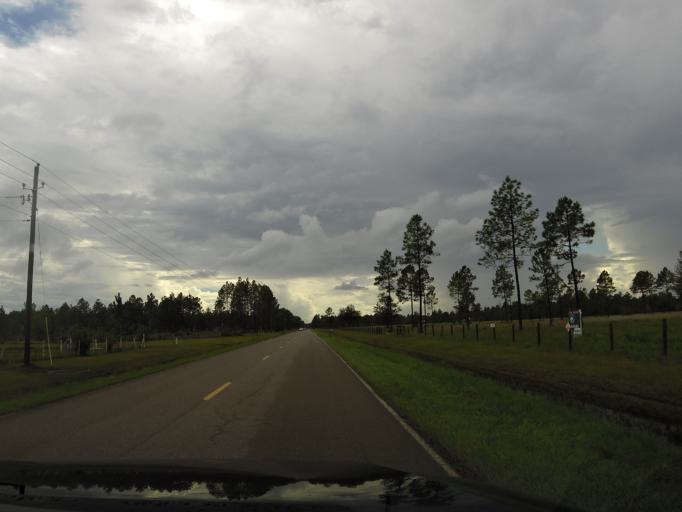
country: US
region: Florida
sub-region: Duval County
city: Baldwin
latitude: 30.4400
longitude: -82.0105
